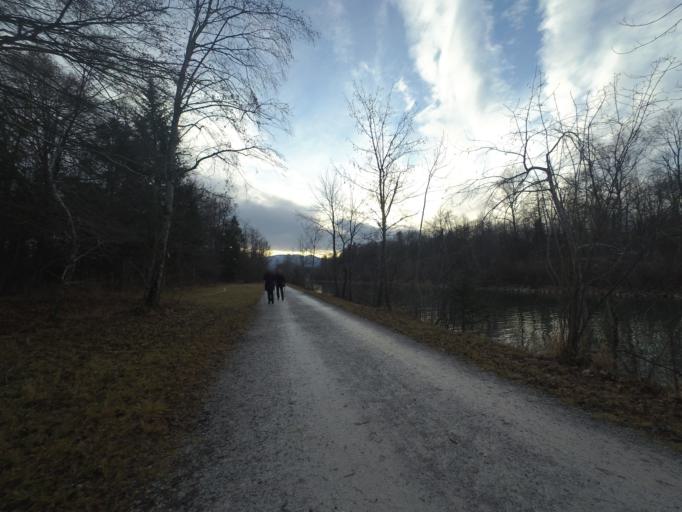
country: DE
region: Bavaria
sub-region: Upper Bavaria
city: Freilassing
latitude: 47.8232
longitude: 12.9818
